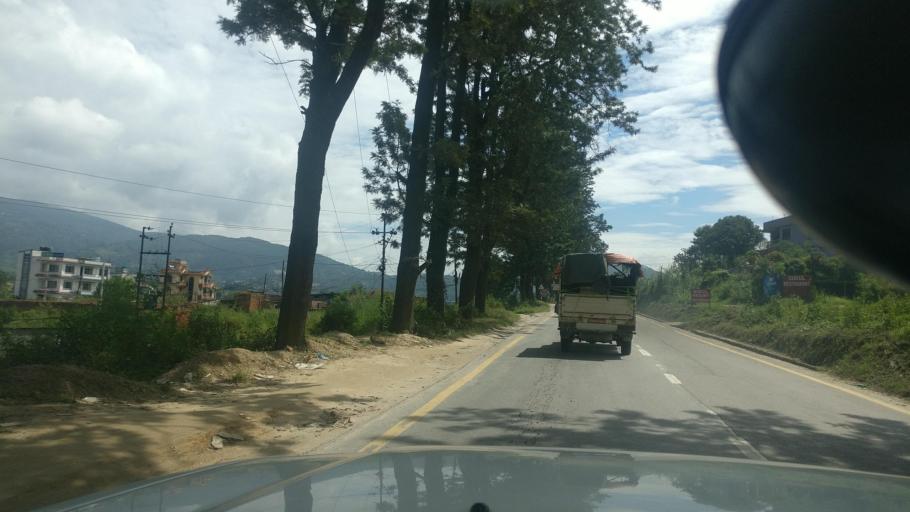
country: NP
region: Central Region
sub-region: Bagmati Zone
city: Bhaktapur
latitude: 27.6599
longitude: 85.4498
